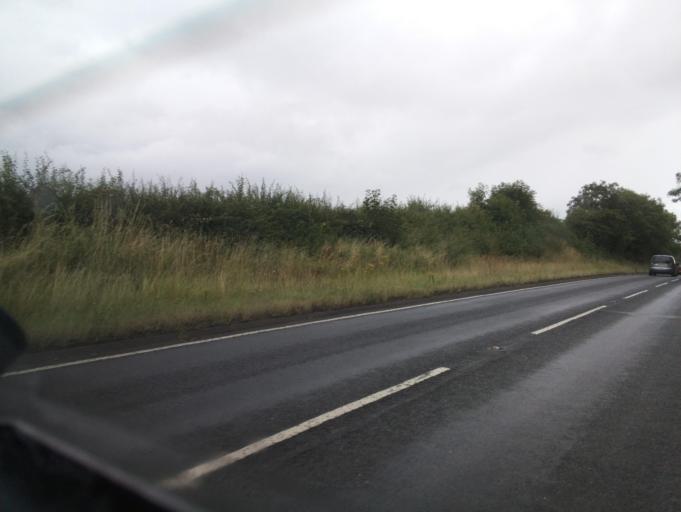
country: GB
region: England
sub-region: Worcestershire
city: Fernhill Heath
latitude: 52.1929
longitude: -2.1494
